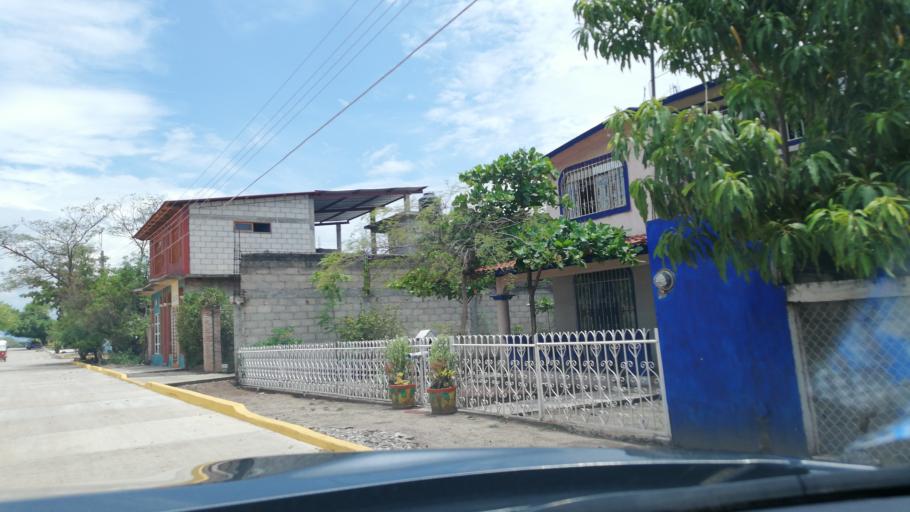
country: MX
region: Oaxaca
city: Santa Maria Jalapa del Marques
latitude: 16.4398
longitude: -95.4386
